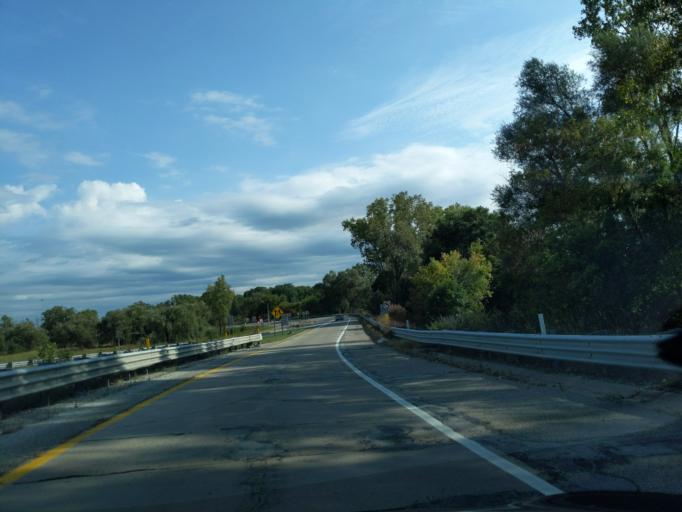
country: US
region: Michigan
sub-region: Ingham County
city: East Lansing
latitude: 42.7231
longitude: -84.5096
